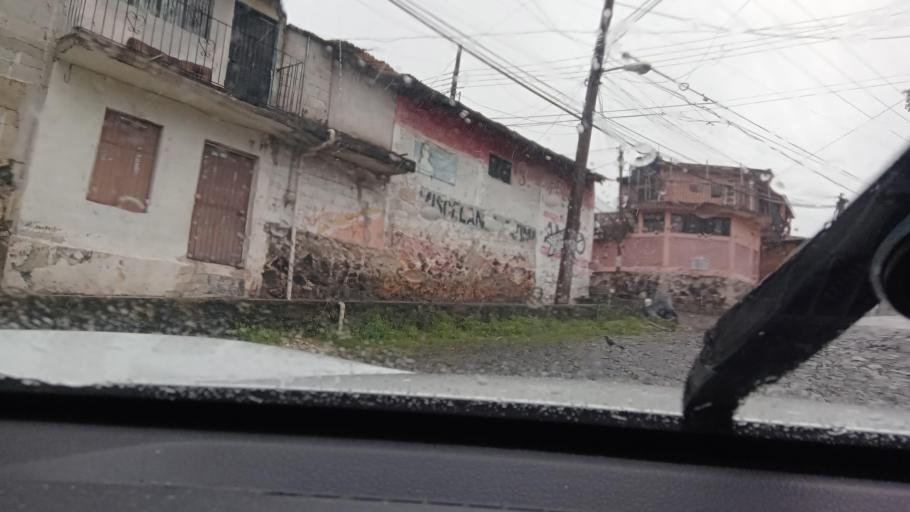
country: MX
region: Veracruz
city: Coatepec
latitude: 19.4586
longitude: -96.9698
